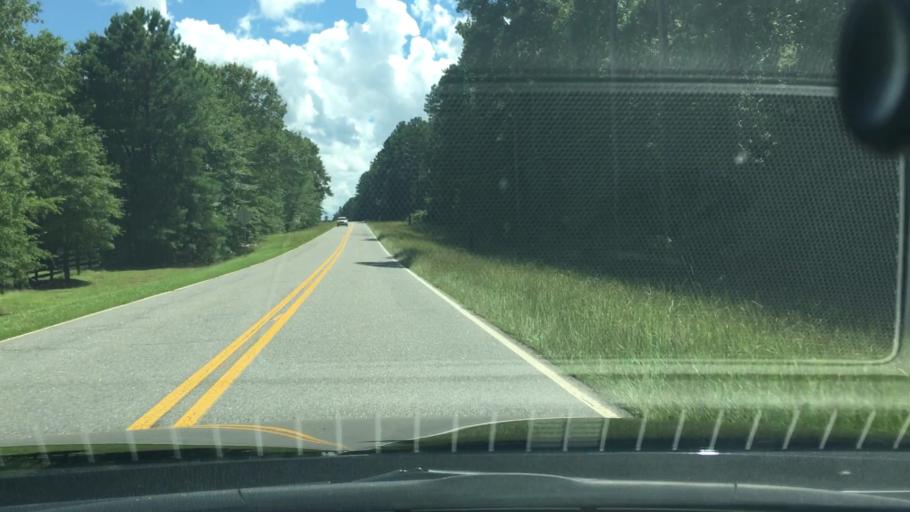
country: US
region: Georgia
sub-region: Putnam County
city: Jefferson
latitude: 33.3749
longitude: -83.2512
